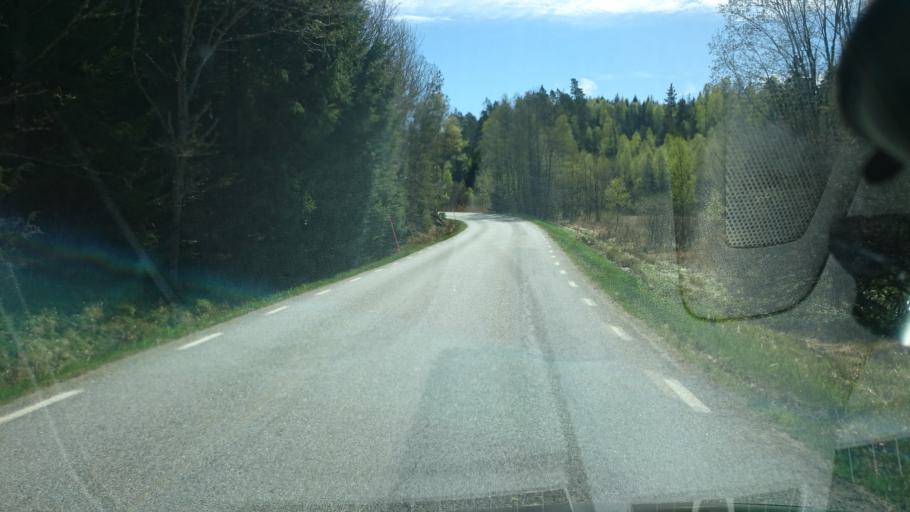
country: SE
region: Vaestra Goetaland
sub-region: Munkedals Kommun
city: Munkedal
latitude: 58.3708
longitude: 11.6908
